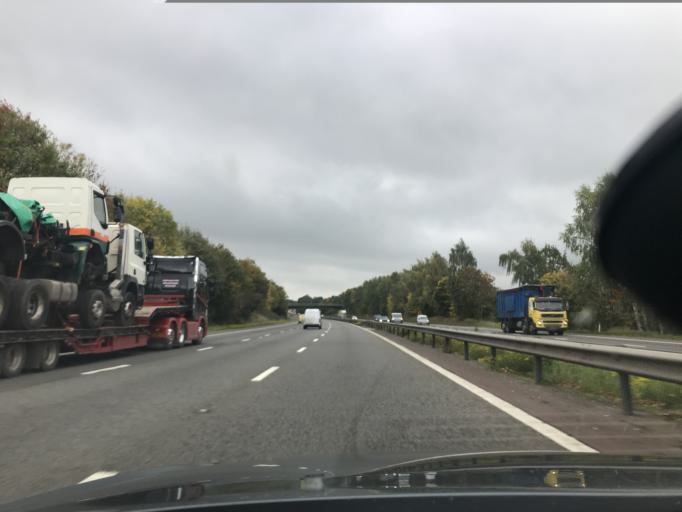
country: GB
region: England
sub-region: Warwickshire
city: Wroxall
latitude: 52.3109
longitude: -1.7102
